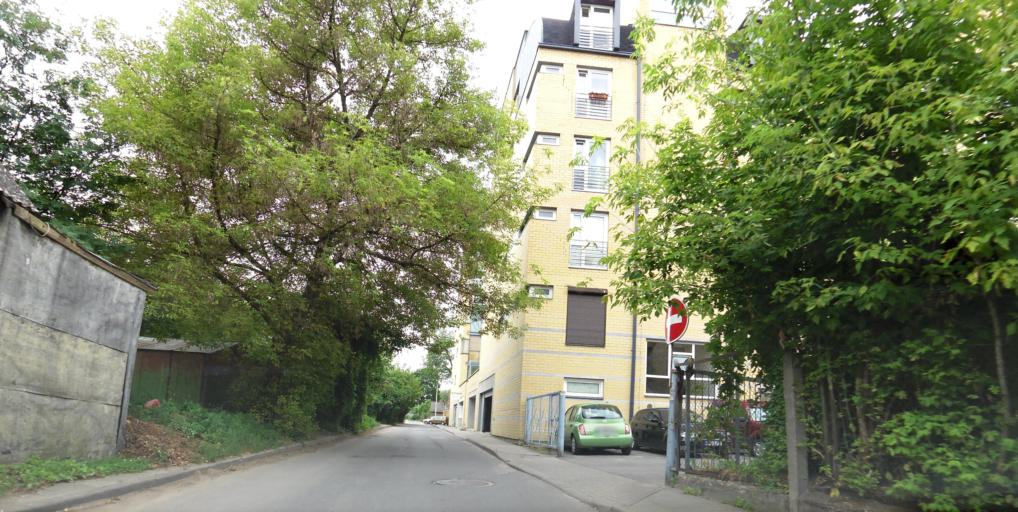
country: LT
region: Vilnius County
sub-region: Vilnius
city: Vilnius
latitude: 54.7025
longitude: 25.2832
